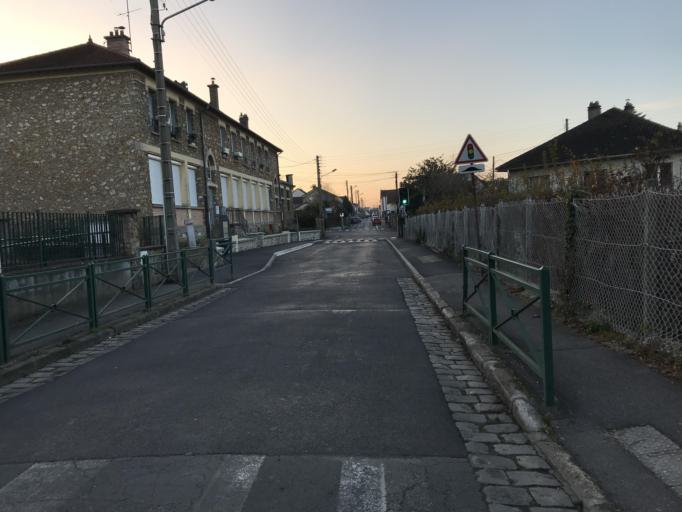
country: FR
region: Ile-de-France
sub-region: Departement de l'Essonne
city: Igny
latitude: 48.7321
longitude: 2.2245
